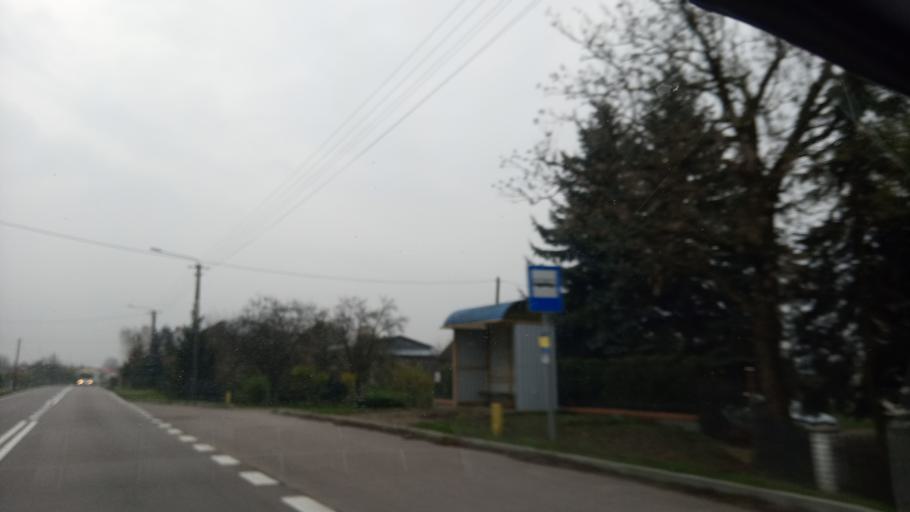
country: PL
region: Pomeranian Voivodeship
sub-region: Powiat czluchowski
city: Czluchow
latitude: 53.6849
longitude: 17.3311
